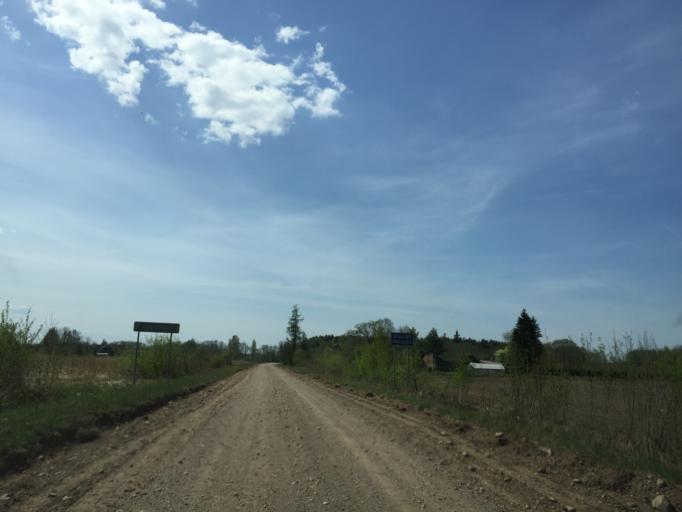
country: LV
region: Limbazu Rajons
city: Limbazi
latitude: 57.3865
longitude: 24.5908
